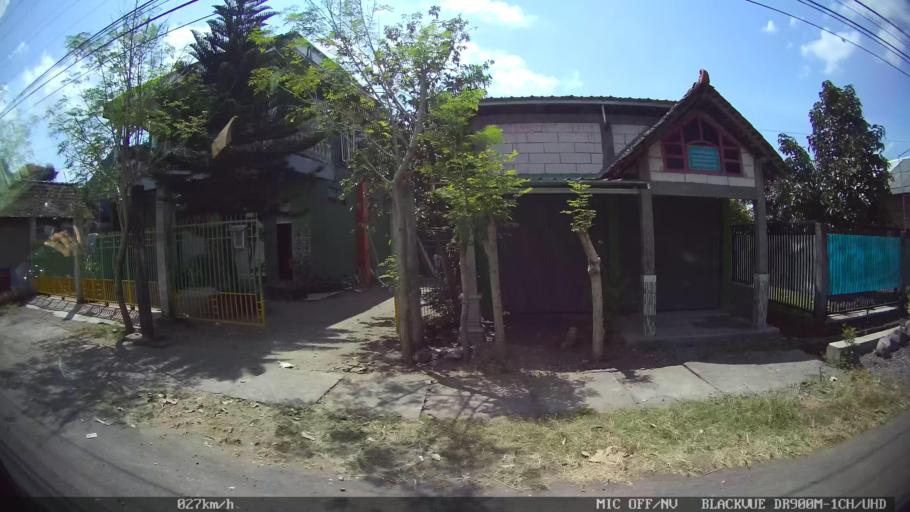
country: ID
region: Daerah Istimewa Yogyakarta
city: Sewon
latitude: -7.8368
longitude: 110.3809
